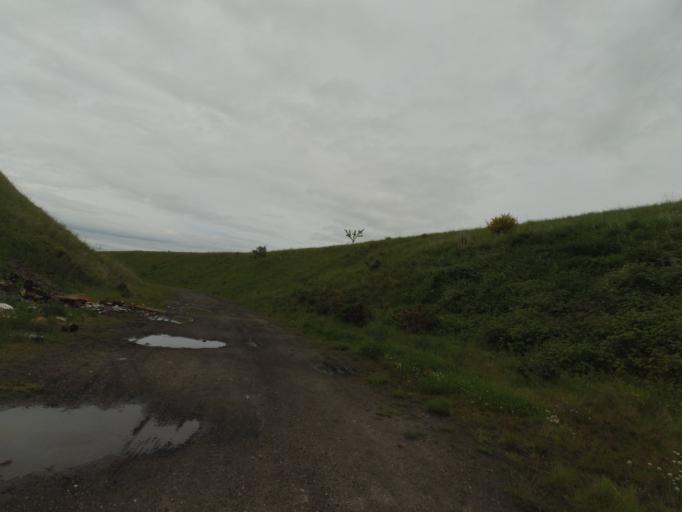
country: GB
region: Scotland
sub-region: East Lothian
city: Macmerry
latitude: 55.9504
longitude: -2.9229
